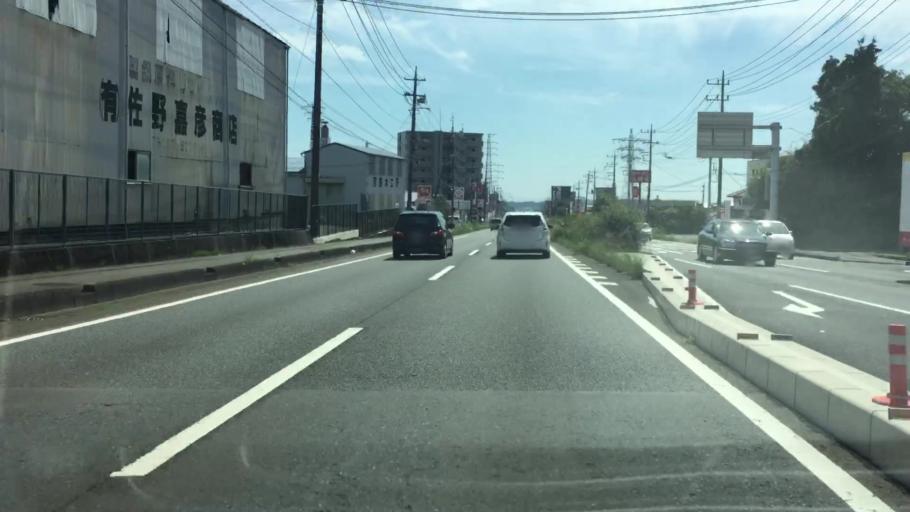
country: JP
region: Shizuoka
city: Fujinomiya
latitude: 35.2449
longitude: 138.6182
